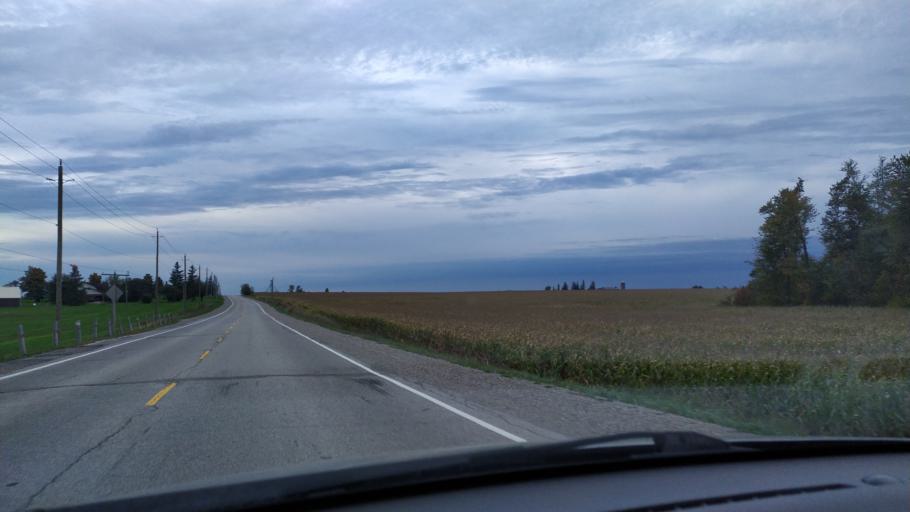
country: CA
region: Ontario
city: Stratford
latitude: 43.5074
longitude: -80.7596
